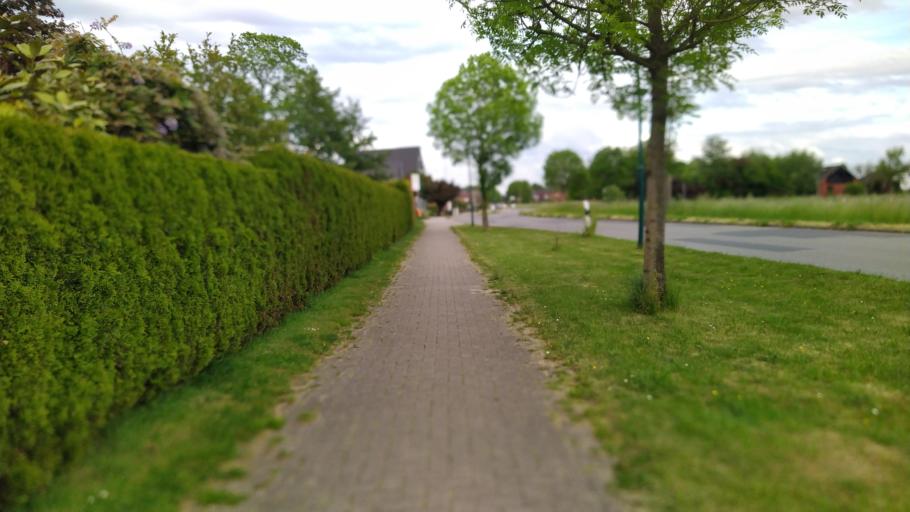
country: DE
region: Lower Saxony
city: Neu Wulmstorf
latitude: 53.4906
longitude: 9.7604
